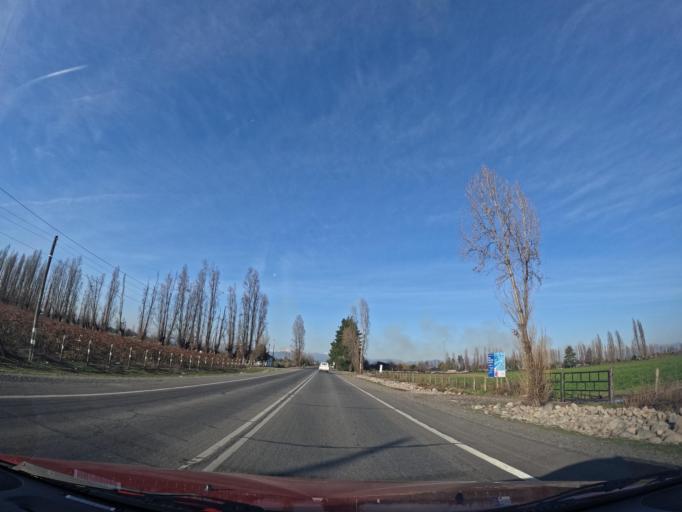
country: CL
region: Maule
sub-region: Provincia de Talca
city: San Clemente
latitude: -35.6271
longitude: -71.4754
